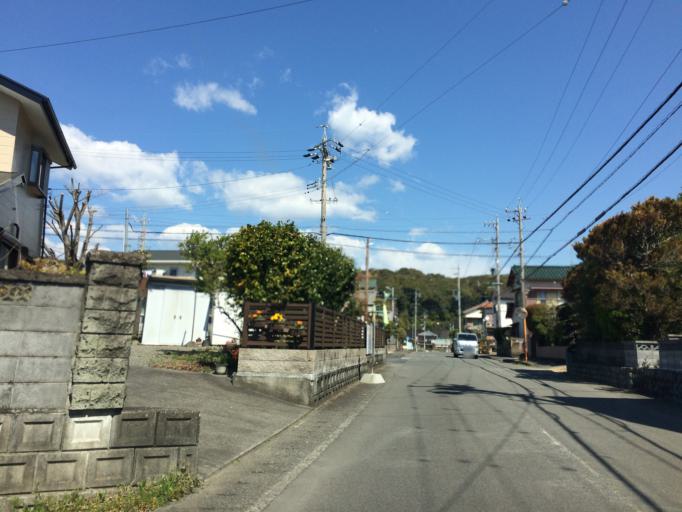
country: JP
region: Shizuoka
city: Fujieda
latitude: 34.8461
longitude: 138.2284
